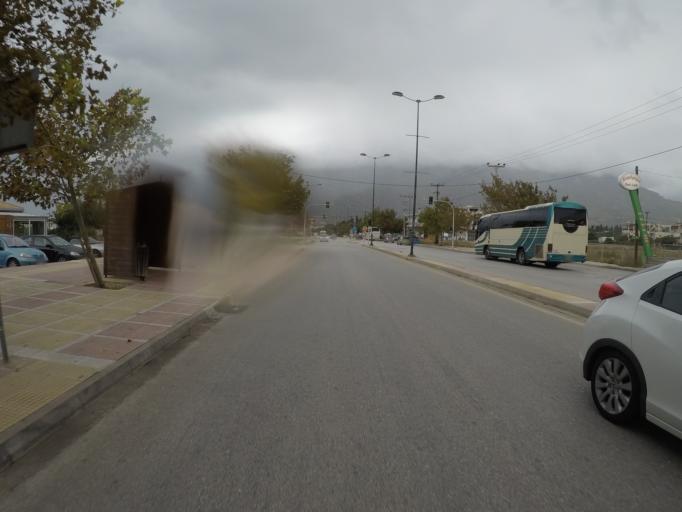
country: GR
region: Peloponnese
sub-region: Nomos Korinthias
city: Loutraki
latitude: 37.9569
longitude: 22.9792
